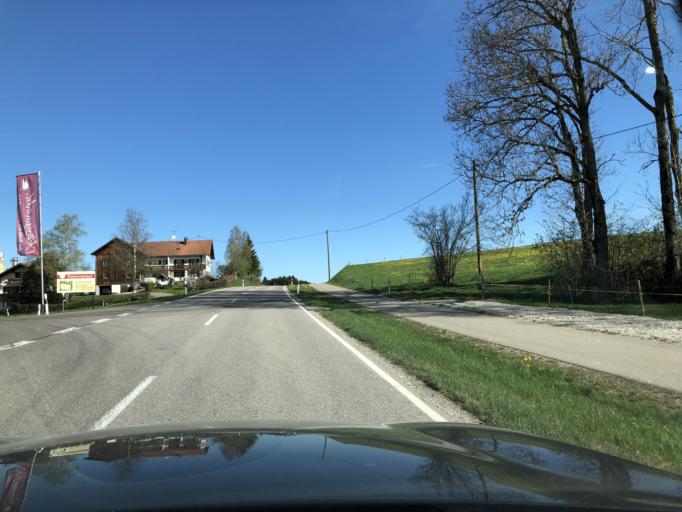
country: DE
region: Bavaria
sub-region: Swabia
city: Ruckholz
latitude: 47.6646
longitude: 10.5421
